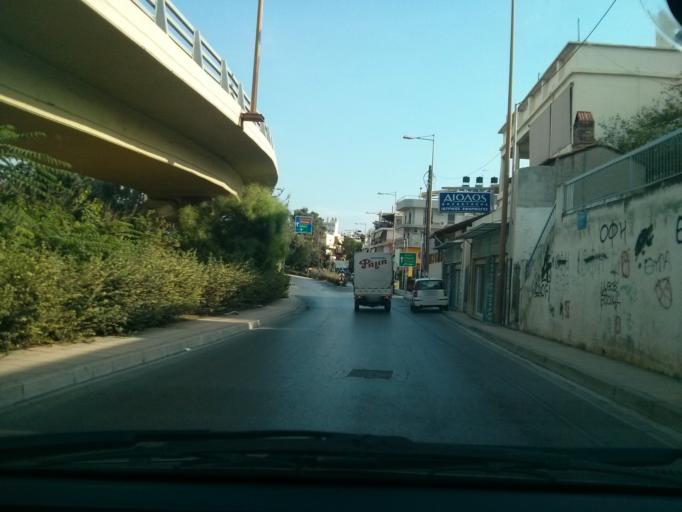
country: GR
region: Crete
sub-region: Nomos Irakleiou
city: Irakleion
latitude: 35.3269
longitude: 25.1382
